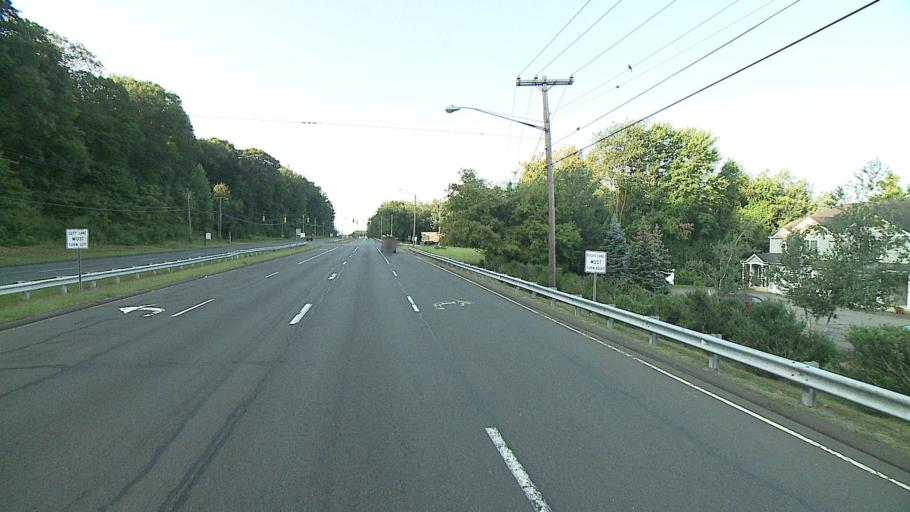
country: US
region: Connecticut
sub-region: Hartford County
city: Kensington
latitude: 41.5787
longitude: -72.7673
